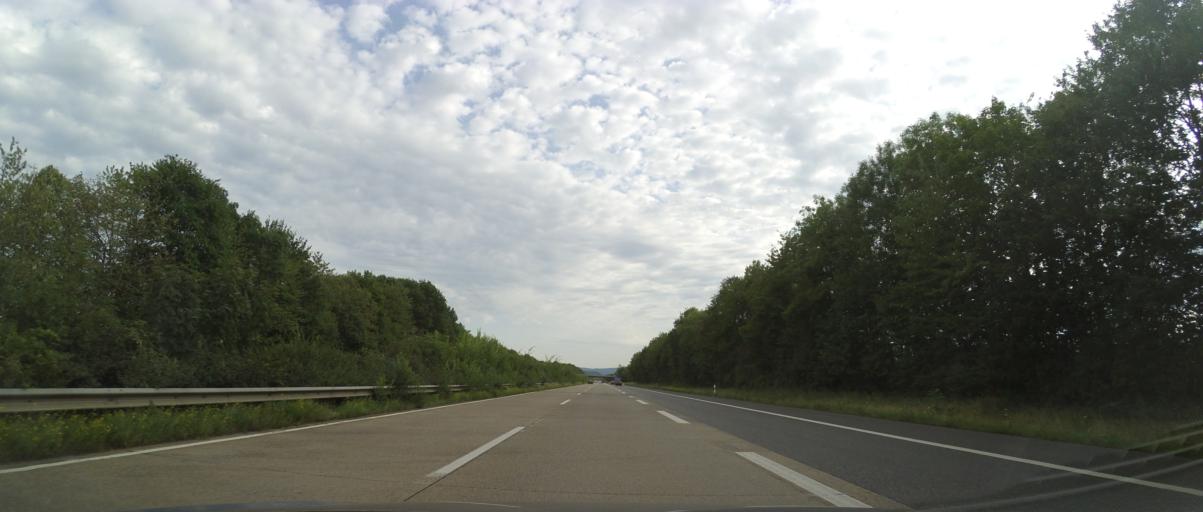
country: DE
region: Rheinland-Pfalz
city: Esch
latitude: 49.9060
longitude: 6.8537
